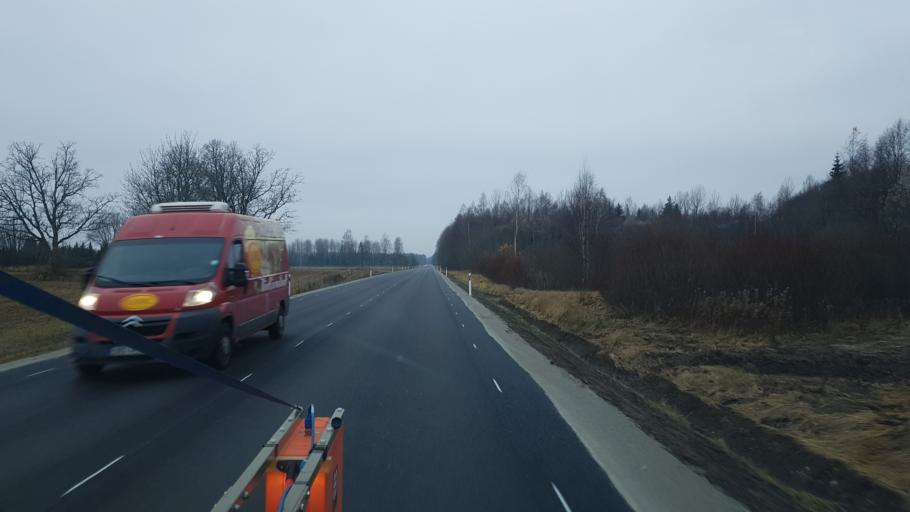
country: EE
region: Paernumaa
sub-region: Vaendra vald (alev)
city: Vandra
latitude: 58.8357
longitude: 25.0841
